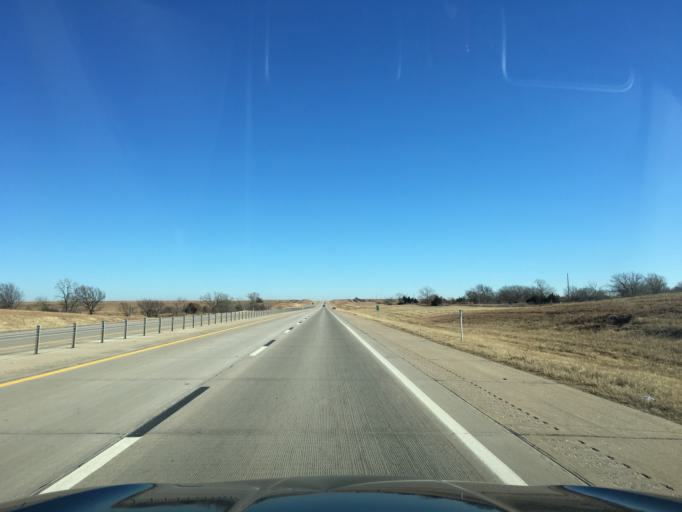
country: US
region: Oklahoma
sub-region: Noble County
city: Perry
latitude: 36.3920
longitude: -97.1691
